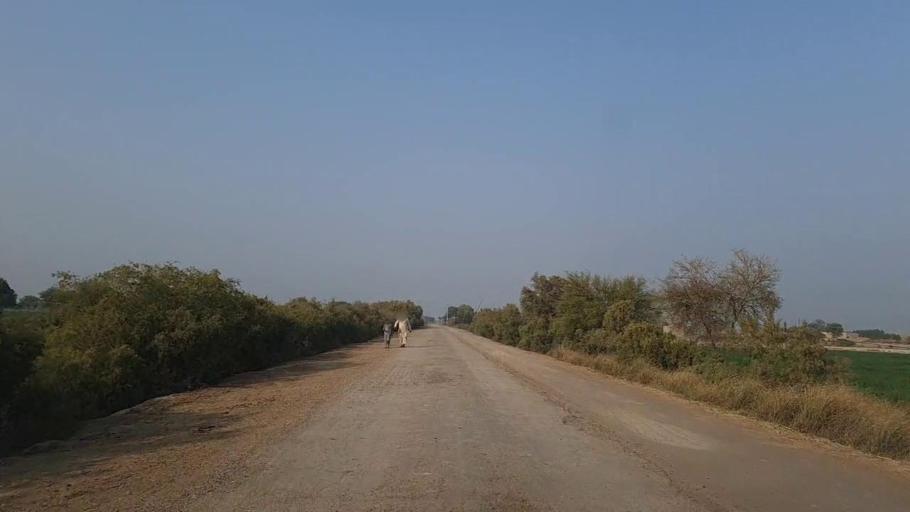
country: PK
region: Sindh
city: Nawabshah
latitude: 26.3395
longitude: 68.4892
